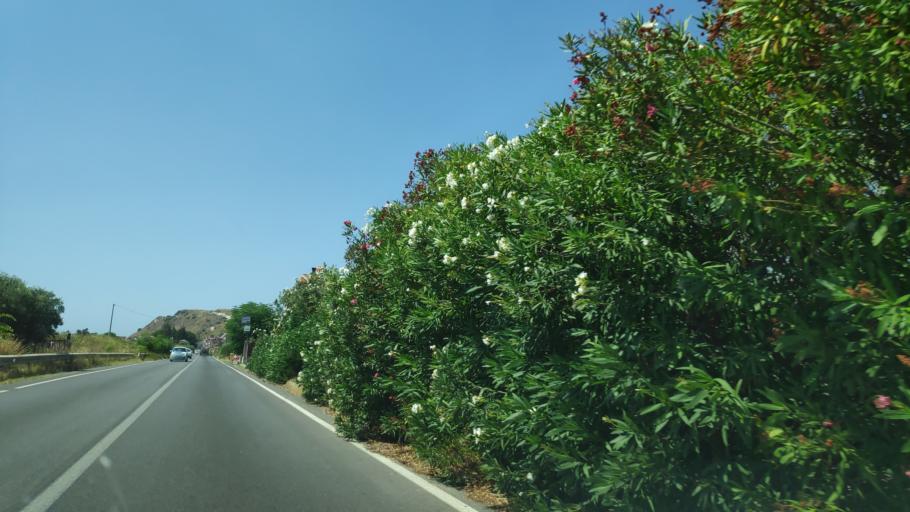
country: IT
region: Calabria
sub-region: Provincia di Reggio Calabria
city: Weather Station
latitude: 37.9353
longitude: 16.0726
